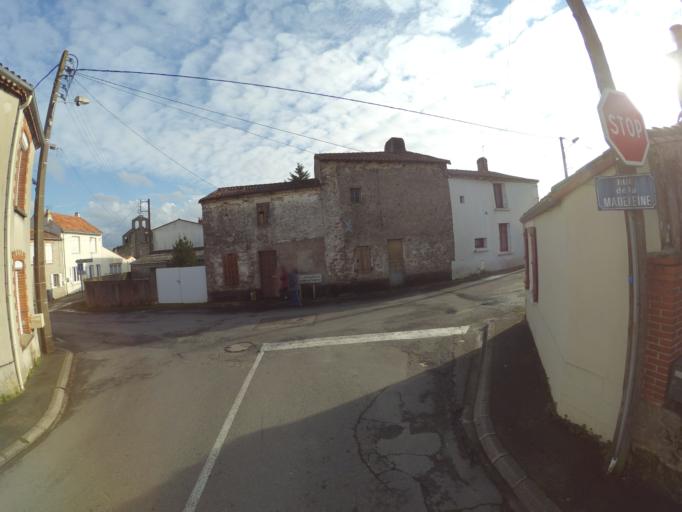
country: FR
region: Pays de la Loire
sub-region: Departement de la Loire-Atlantique
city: Clisson
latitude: 47.0808
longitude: -1.2767
